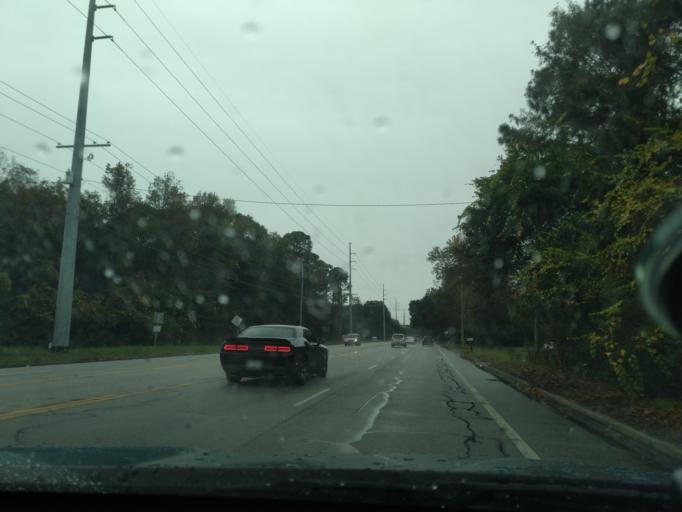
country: US
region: South Carolina
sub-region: Charleston County
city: Folly Beach
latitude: 32.7028
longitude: -79.9661
